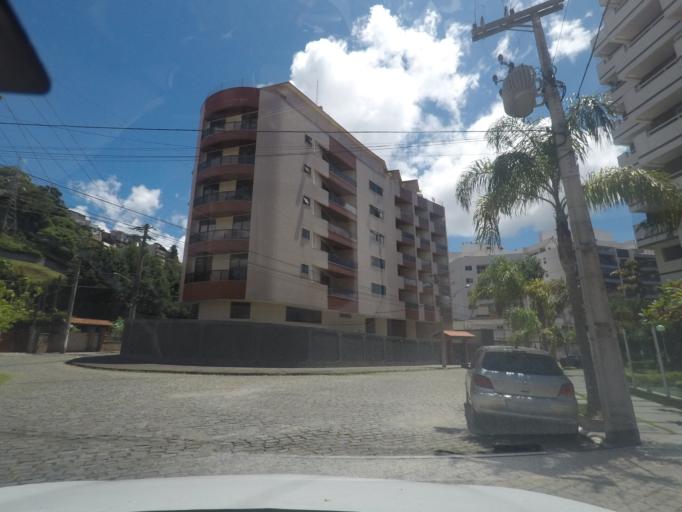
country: BR
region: Rio de Janeiro
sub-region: Teresopolis
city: Teresopolis
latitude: -22.4209
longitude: -42.9796
